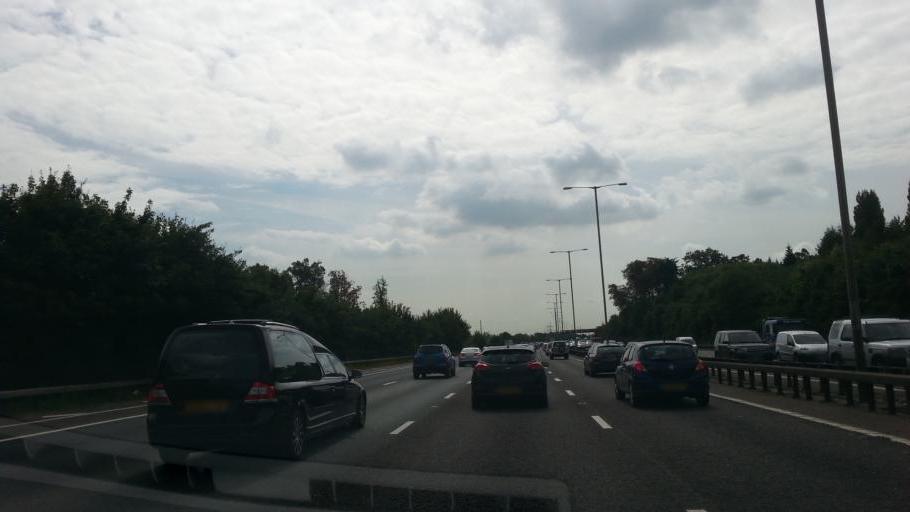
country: GB
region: England
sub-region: Greater London
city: Uxbridge
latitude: 51.5395
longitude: -0.5018
